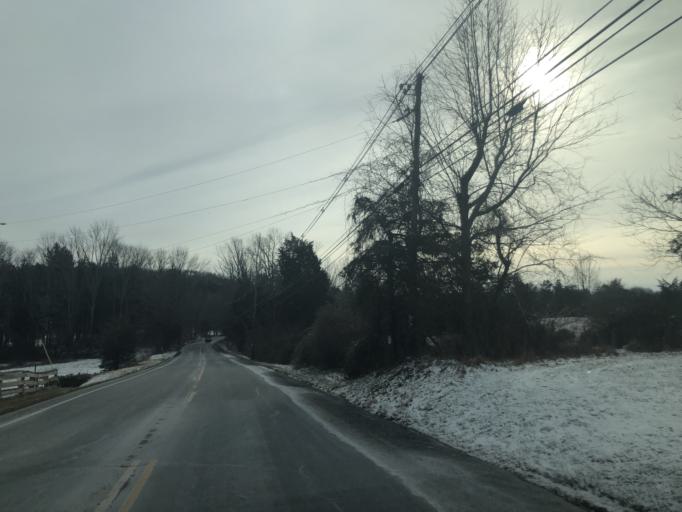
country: US
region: New Jersey
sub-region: Warren County
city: Oxford
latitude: 40.9221
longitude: -74.9907
